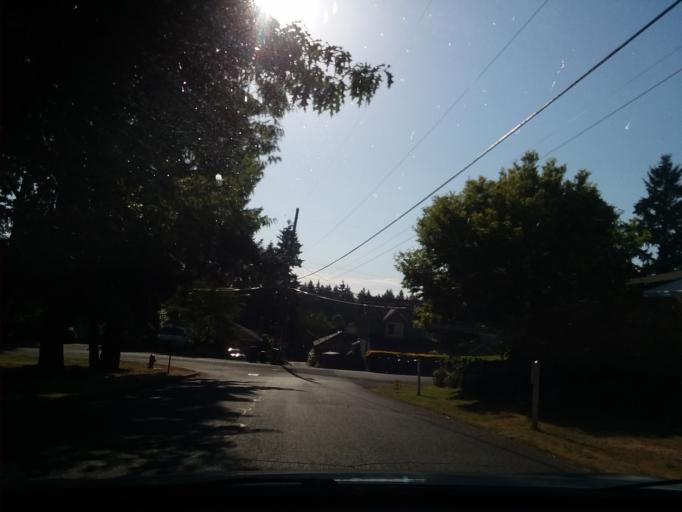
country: US
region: Washington
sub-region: King County
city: Shoreline
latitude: 47.7268
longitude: -122.3268
